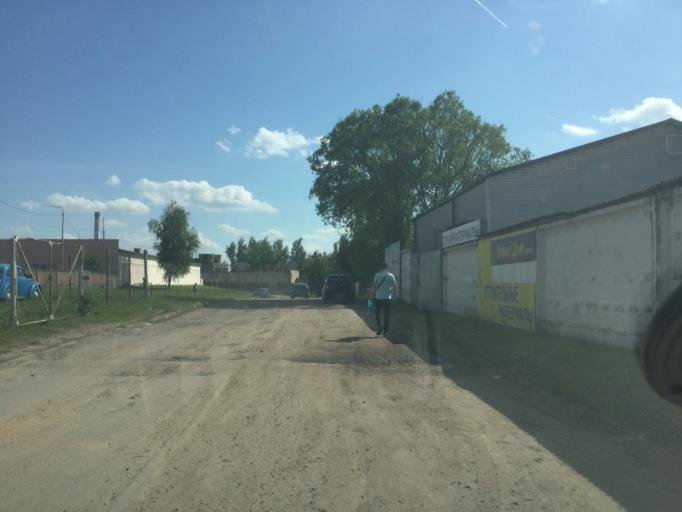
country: BY
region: Vitebsk
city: Vitebsk
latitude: 55.1656
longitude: 30.2425
